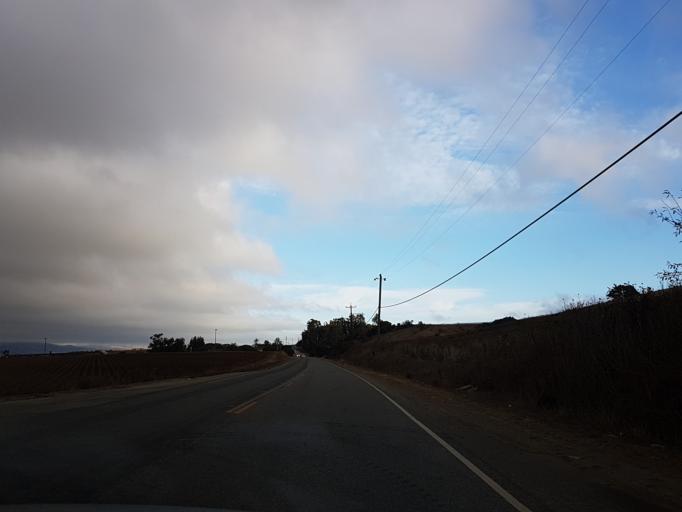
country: US
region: California
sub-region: Monterey County
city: Salinas
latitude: 36.5956
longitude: -121.6195
